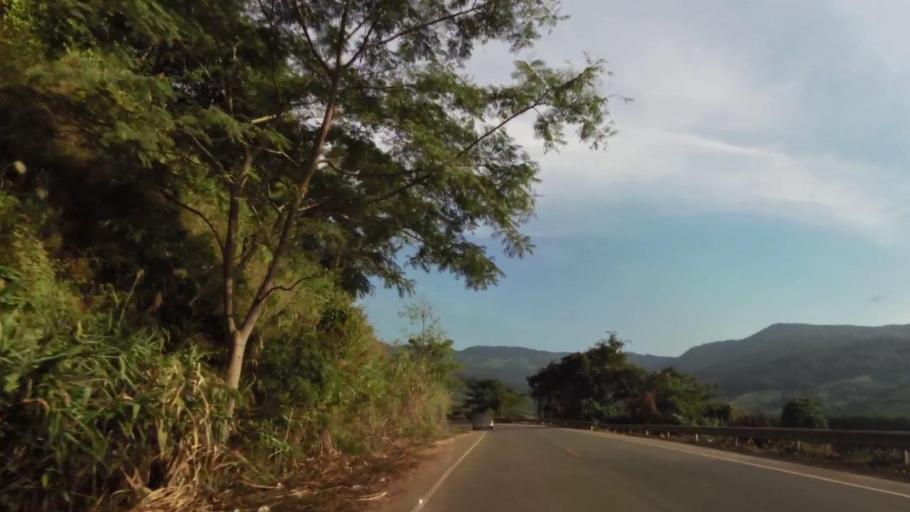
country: TH
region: Chiang Rai
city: Khun Tan
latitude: 19.8676
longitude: 100.4067
